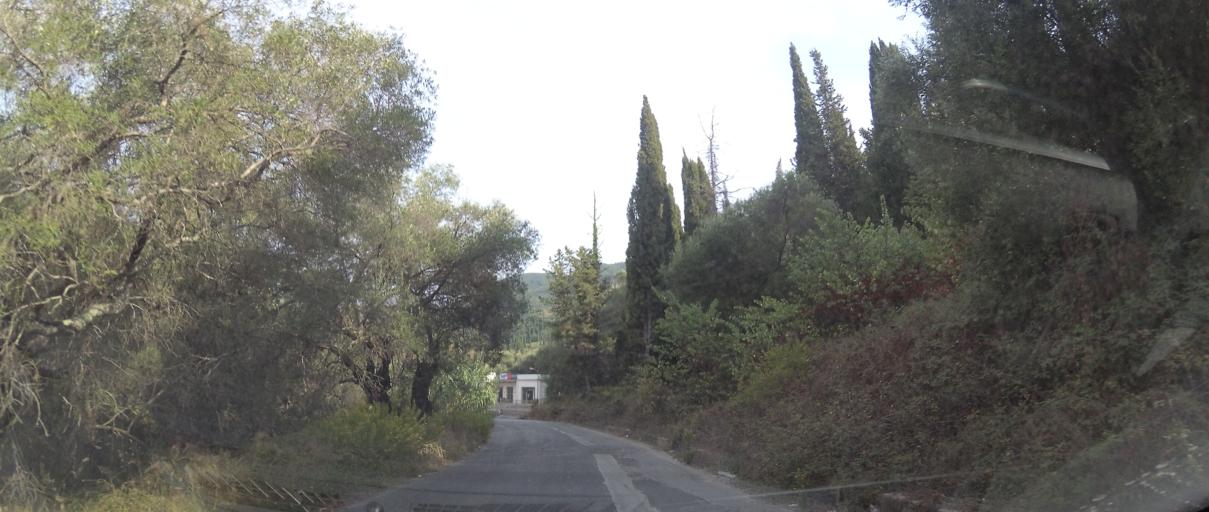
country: GR
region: Ionian Islands
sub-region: Nomos Kerkyras
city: Kynopiastes
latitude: 39.5561
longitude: 19.8601
